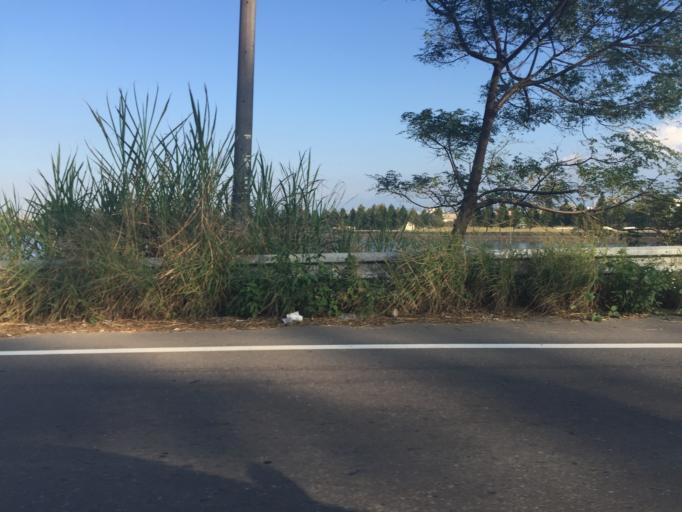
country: TW
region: Taiwan
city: Daxi
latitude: 24.9129
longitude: 121.2543
